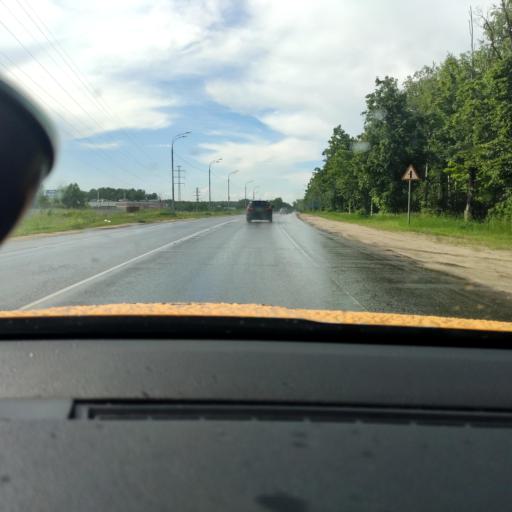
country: RU
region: Moskovskaya
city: Stupino
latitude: 54.9115
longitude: 38.0697
